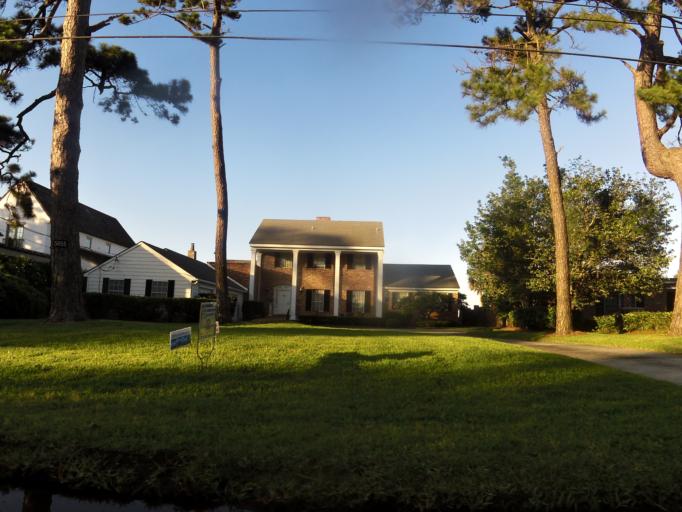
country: US
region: Florida
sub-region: Duval County
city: Jacksonville
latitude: 30.2552
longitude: -81.6915
